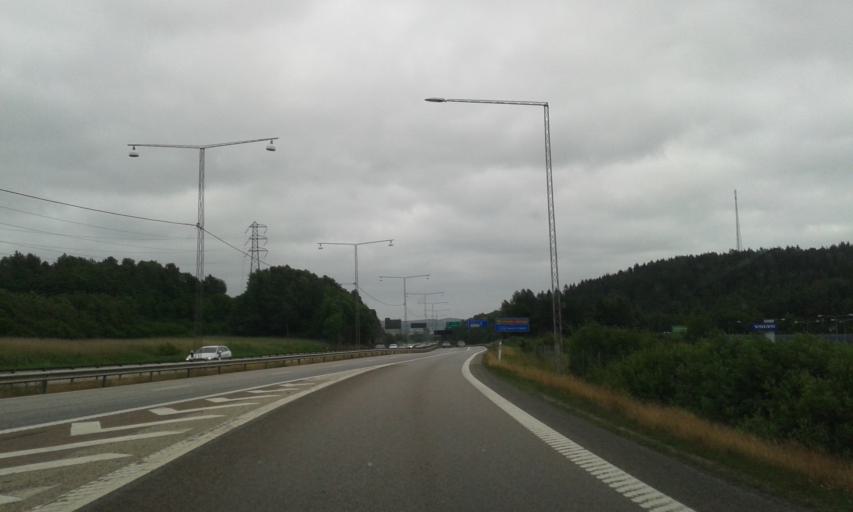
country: SE
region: Vaestra Goetaland
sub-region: Kungalvs Kommun
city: Kungalv
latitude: 57.8825
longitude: 11.9481
